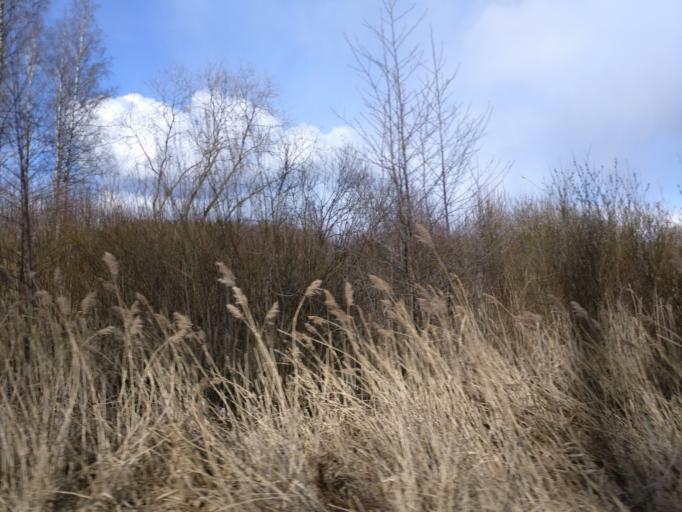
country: FI
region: Varsinais-Suomi
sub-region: Salo
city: Suomusjaervi
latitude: 60.3365
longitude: 23.7012
